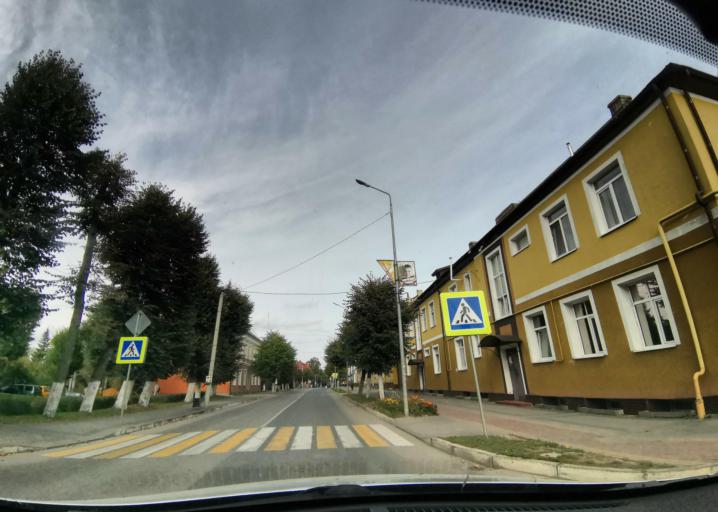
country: RU
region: Kaliningrad
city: Gusev
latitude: 54.5868
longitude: 22.2047
